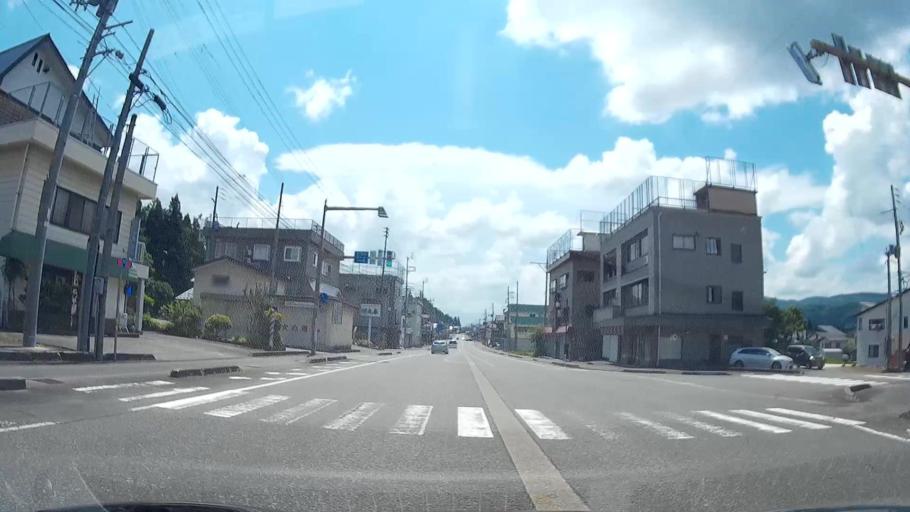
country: JP
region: Niigata
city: Tokamachi
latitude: 37.0966
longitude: 138.7314
